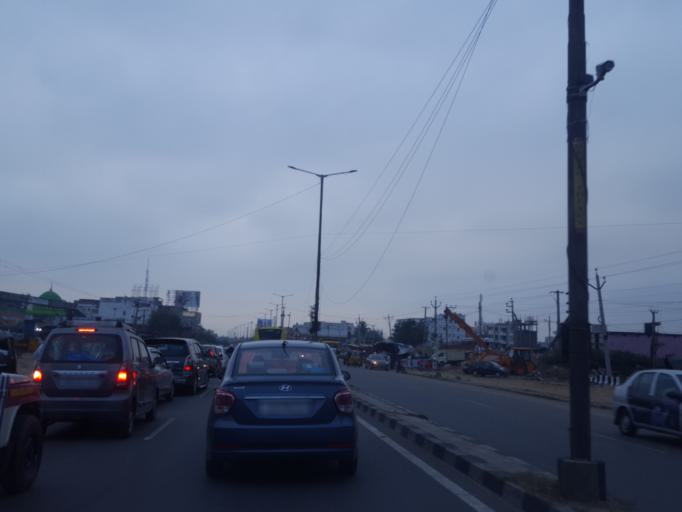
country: IN
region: Telangana
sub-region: Medak
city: Patancheru
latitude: 17.5301
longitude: 78.2600
